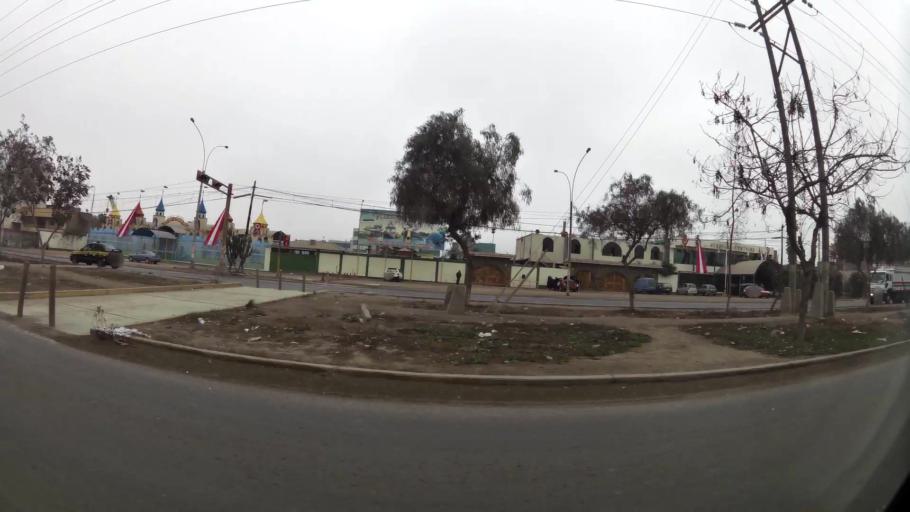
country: PE
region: Lima
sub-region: Lima
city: Urb. Santo Domingo
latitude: -11.9259
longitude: -77.0651
